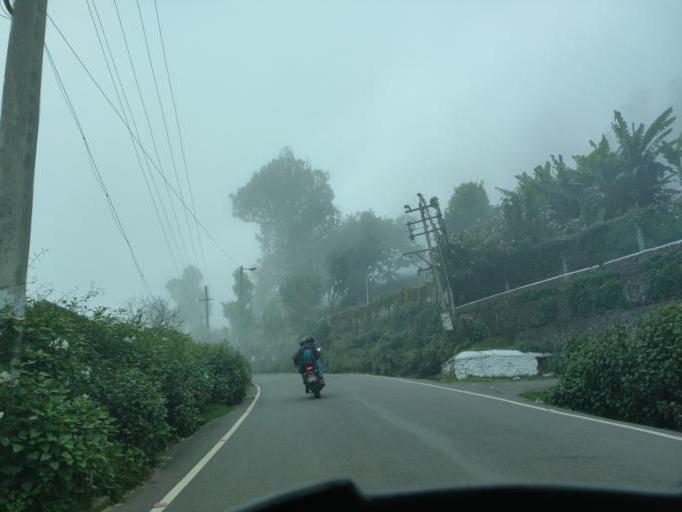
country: IN
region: Tamil Nadu
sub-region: Dindigul
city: Kodaikanal
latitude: 10.2366
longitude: 77.4826
